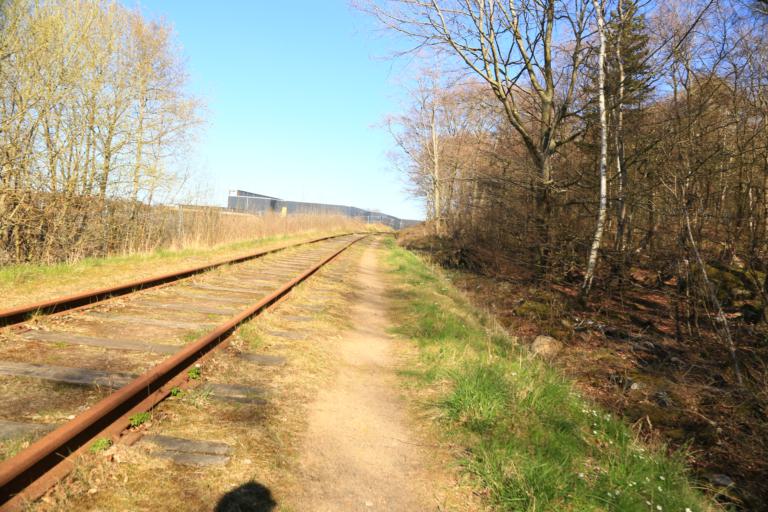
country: SE
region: Halland
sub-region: Varbergs Kommun
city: Varberg
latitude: 57.1214
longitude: 12.2657
